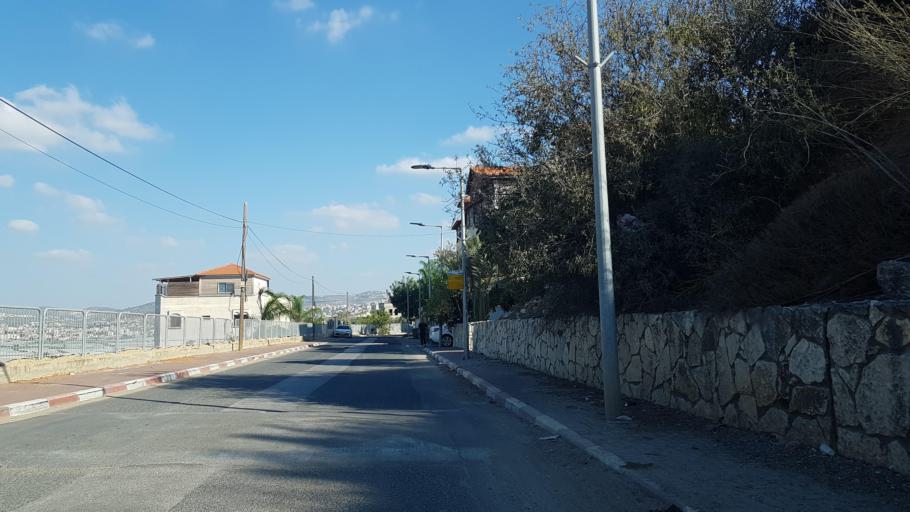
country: PS
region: West Bank
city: Zayta
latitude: 32.3688
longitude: 35.0420
